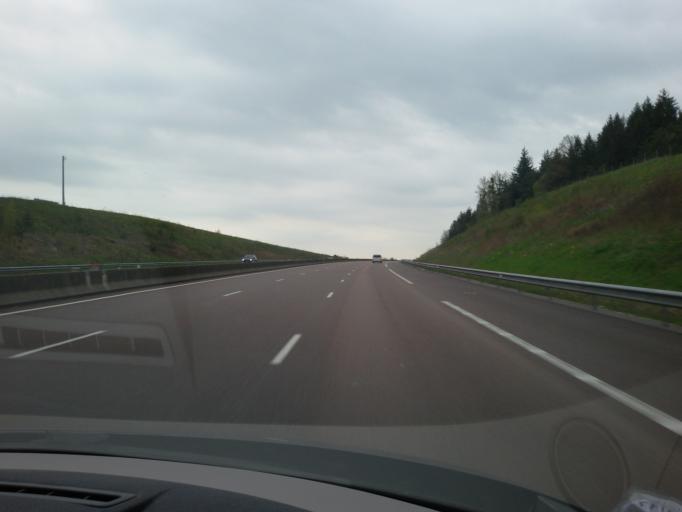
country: FR
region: Champagne-Ardenne
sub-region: Departement de la Haute-Marne
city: Rolampont
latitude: 47.8719
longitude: 5.2199
